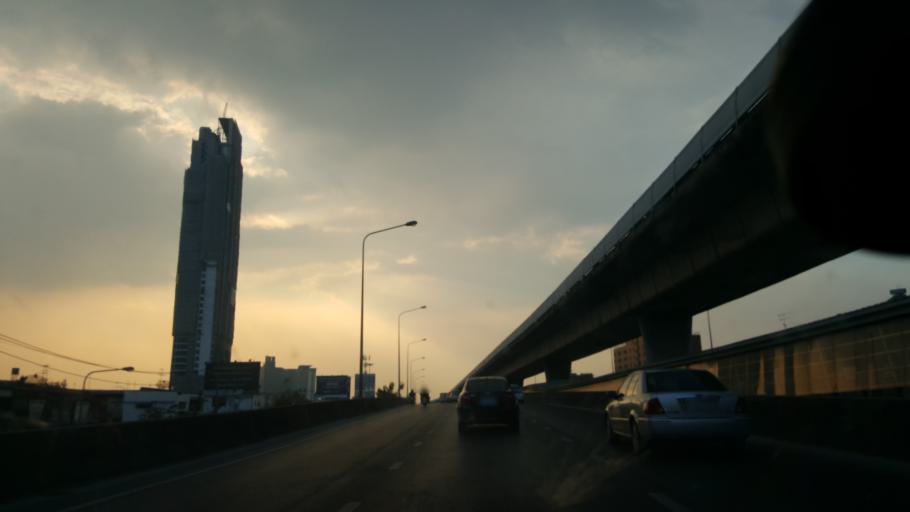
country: TH
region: Bangkok
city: Thon Buri
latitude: 13.7208
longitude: 100.4929
